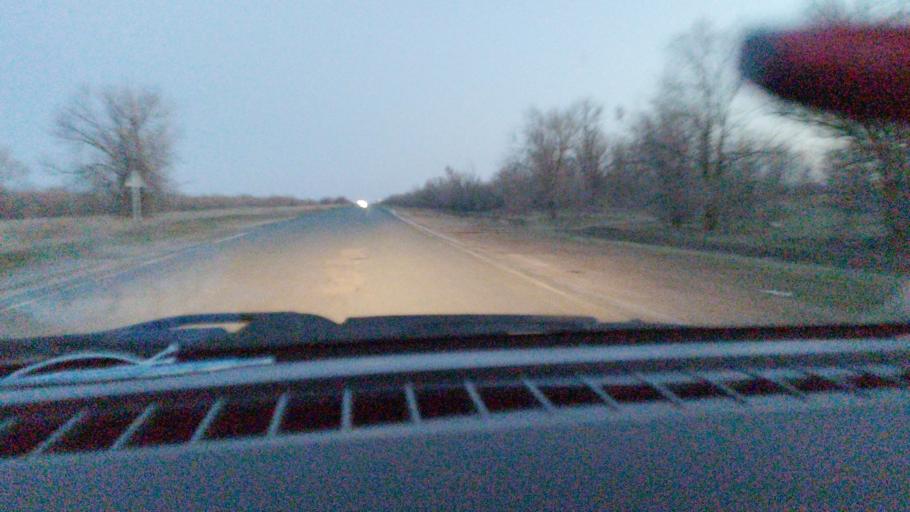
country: RU
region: Saratov
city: Rovnoye
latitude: 50.9774
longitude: 46.1170
